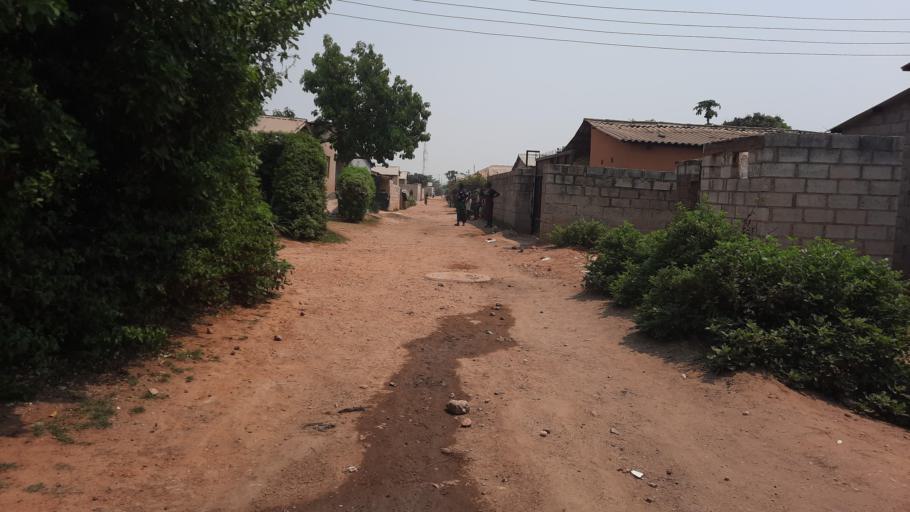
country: ZM
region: Lusaka
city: Lusaka
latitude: -15.3993
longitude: 28.3793
